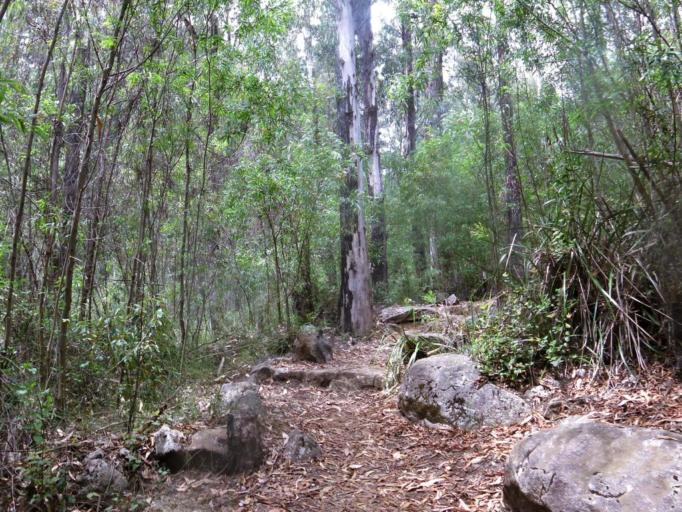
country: AU
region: Victoria
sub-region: Yarra Ranges
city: Healesville
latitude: -37.4582
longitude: 145.5728
